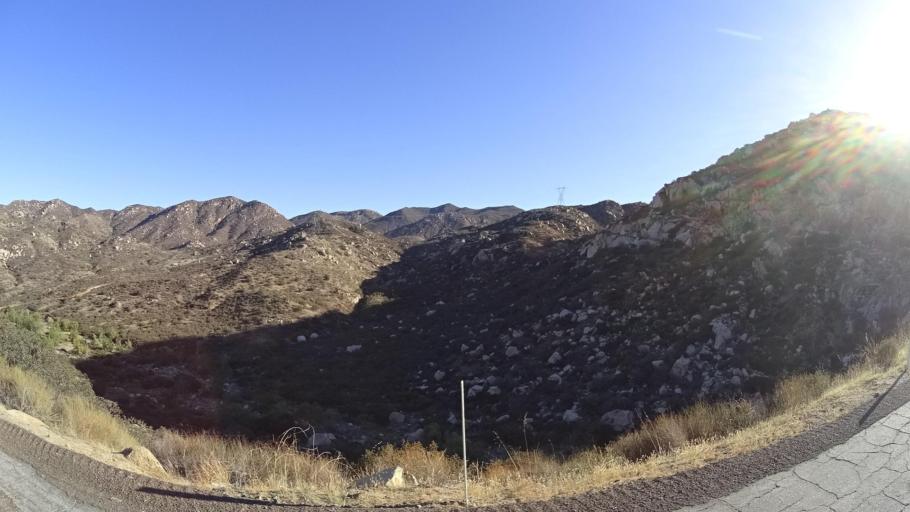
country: MX
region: Baja California
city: Tecate
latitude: 32.6007
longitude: -116.6803
